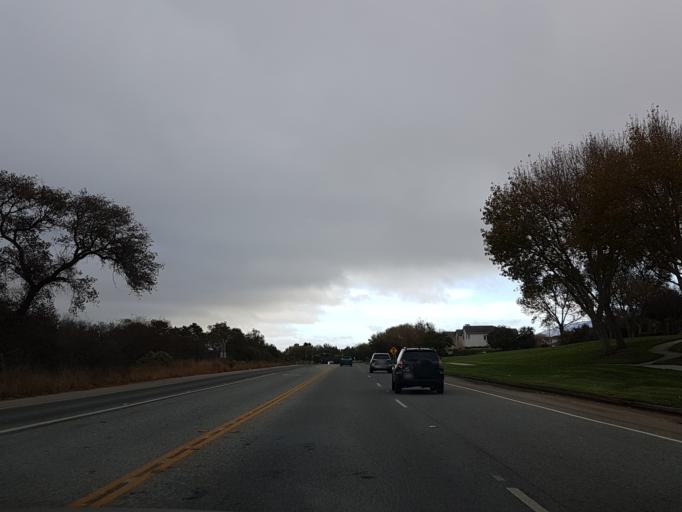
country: US
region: California
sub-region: Monterey County
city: Salinas
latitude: 36.6090
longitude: -121.6493
